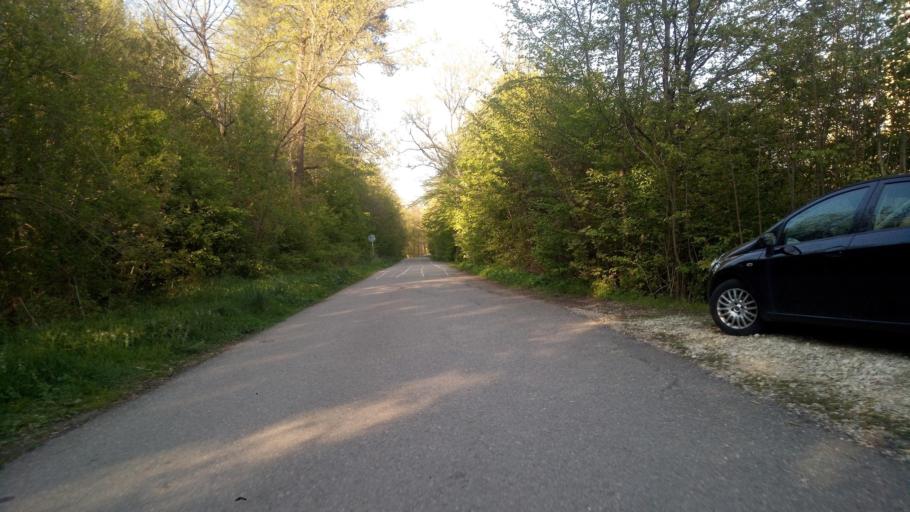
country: DE
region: Baden-Wuerttemberg
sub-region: Regierungsbezirk Stuttgart
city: Goeppingen
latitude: 48.7155
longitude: 9.6792
